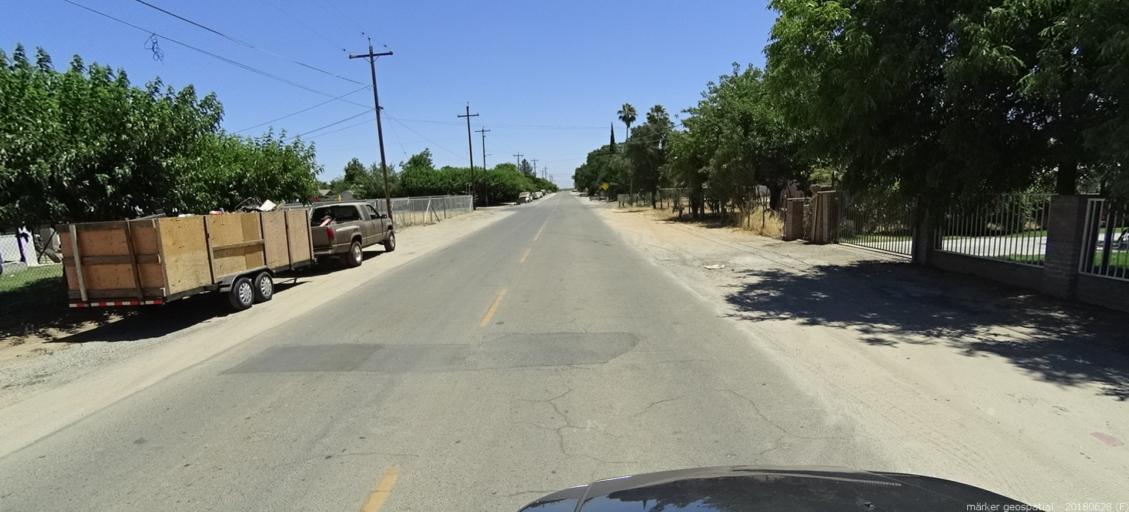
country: US
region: California
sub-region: Madera County
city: Parksdale
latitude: 36.9453
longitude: -120.0157
